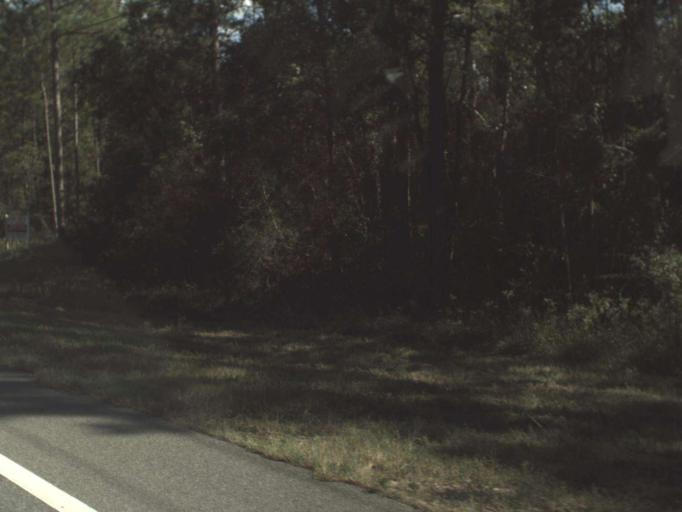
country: US
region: Florida
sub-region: Walton County
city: Freeport
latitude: 30.4767
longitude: -86.0345
